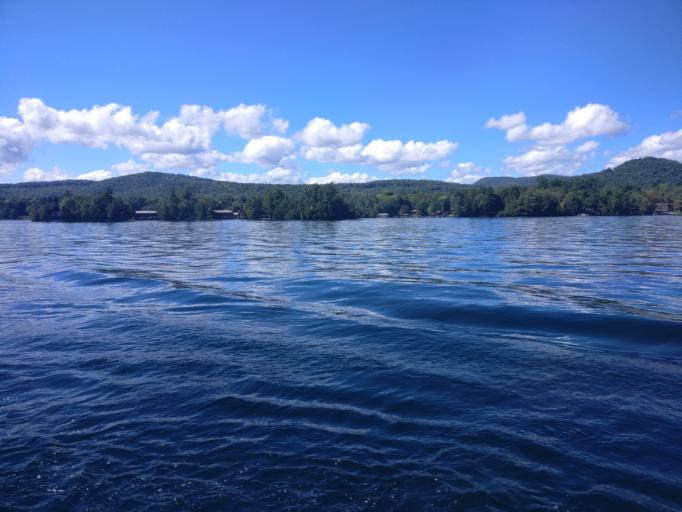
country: US
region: New York
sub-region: Warren County
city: Warrensburg
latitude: 43.5361
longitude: -73.6478
